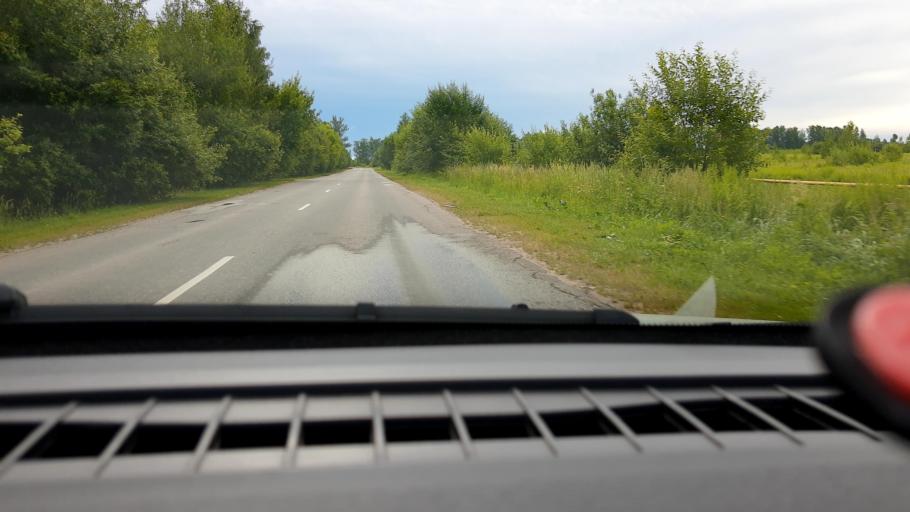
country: RU
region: Nizjnij Novgorod
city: Kstovo
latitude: 56.1493
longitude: 44.3028
